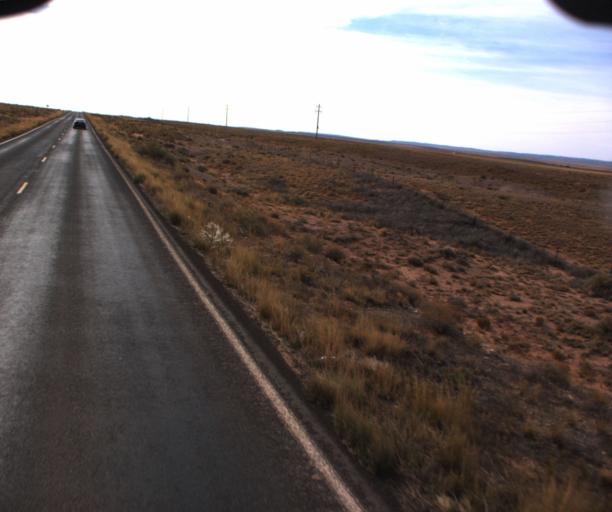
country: US
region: Arizona
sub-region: Apache County
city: Chinle
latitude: 35.9782
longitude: -109.5997
